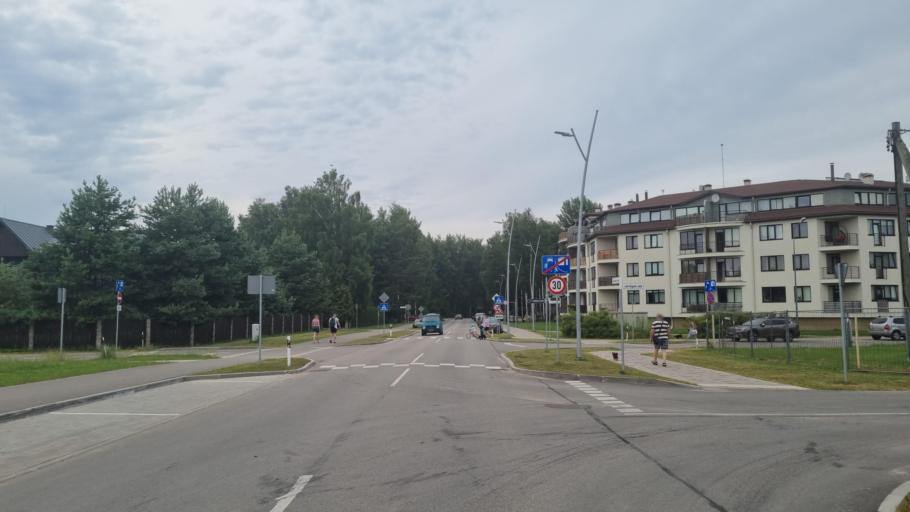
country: LV
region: Kekava
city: Balozi
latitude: 56.8773
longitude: 24.1472
